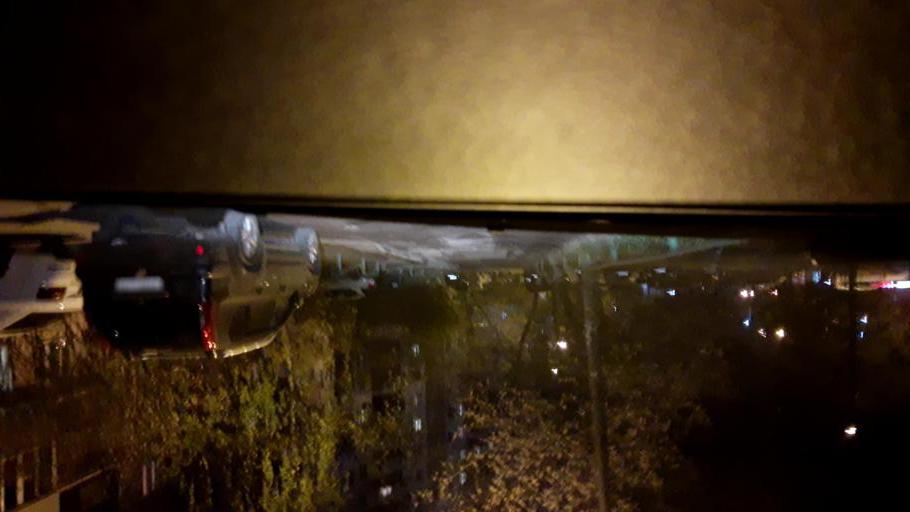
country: RU
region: Nizjnij Novgorod
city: Nizhniy Novgorod
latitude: 56.2950
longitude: 43.9433
